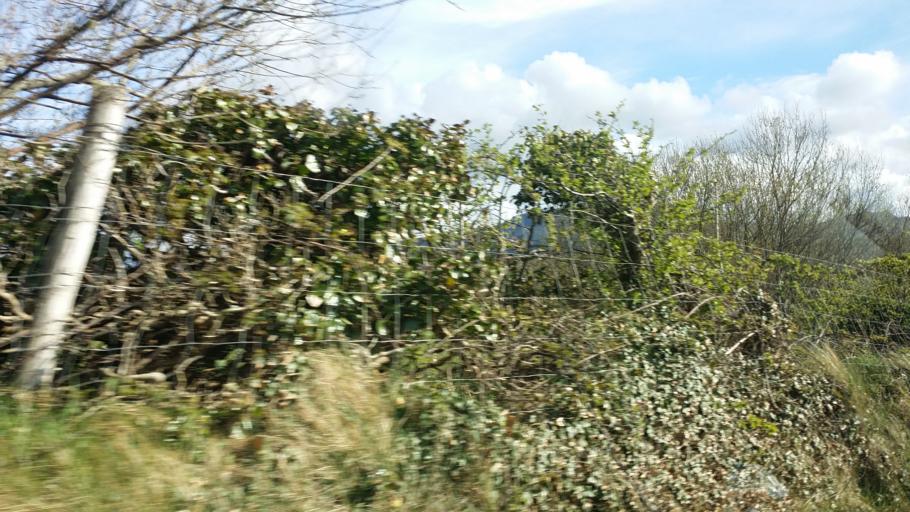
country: IE
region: Ulster
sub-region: County Donegal
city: Bundoran
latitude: 54.4663
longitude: -8.2806
